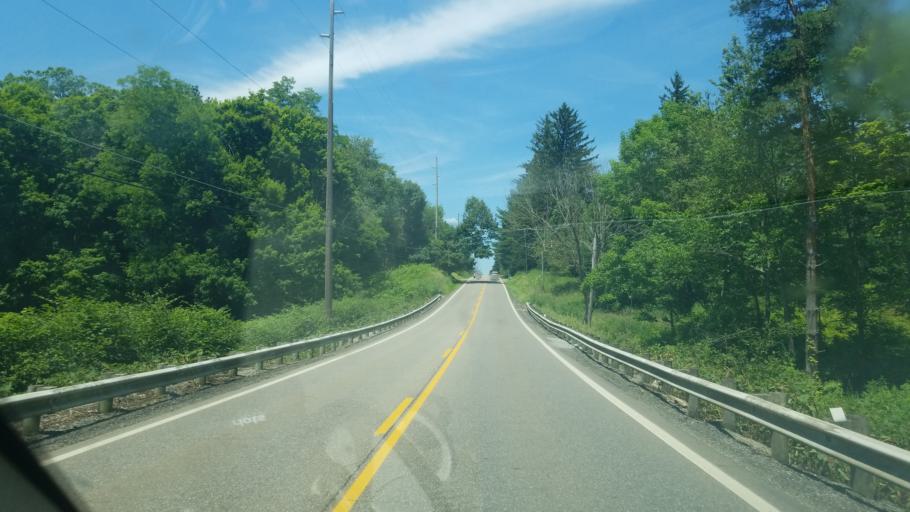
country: US
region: Ohio
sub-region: Columbiana County
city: Lisbon
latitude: 40.8066
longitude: -80.7891
